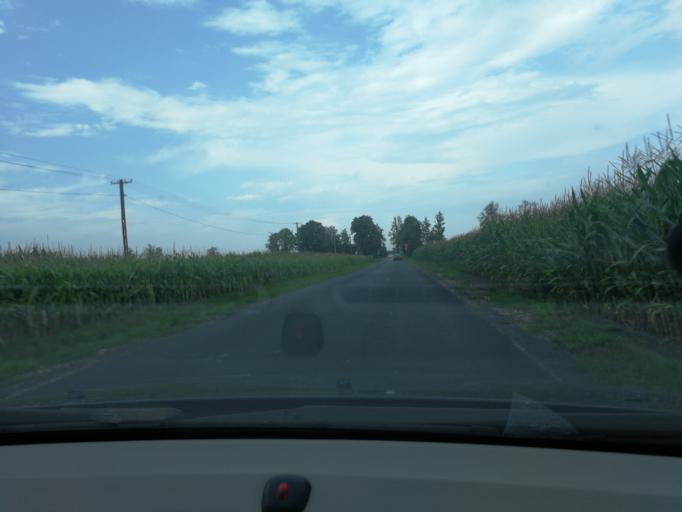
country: PL
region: Masovian Voivodeship
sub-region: Powiat grodziski
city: Grodzisk Mazowiecki
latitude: 52.1301
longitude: 20.5866
